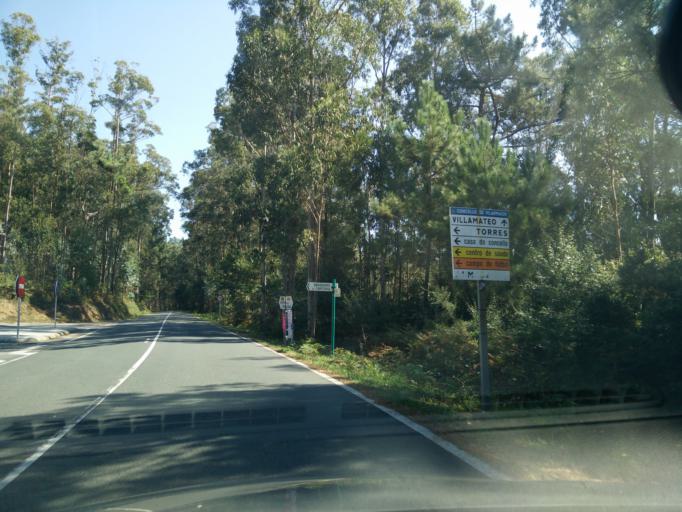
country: ES
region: Galicia
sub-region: Provincia da Coruna
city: Mino
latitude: 43.3392
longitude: -8.1499
